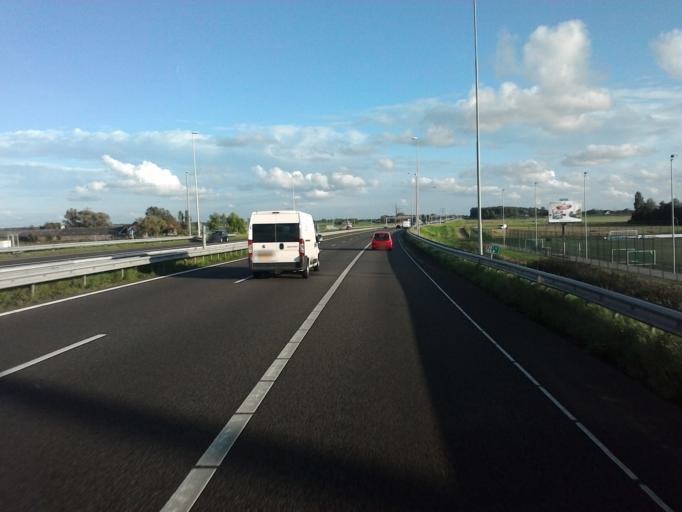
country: NL
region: North Holland
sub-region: Gemeente Velsen
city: Velsen-Zuid
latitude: 52.4172
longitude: 4.6964
